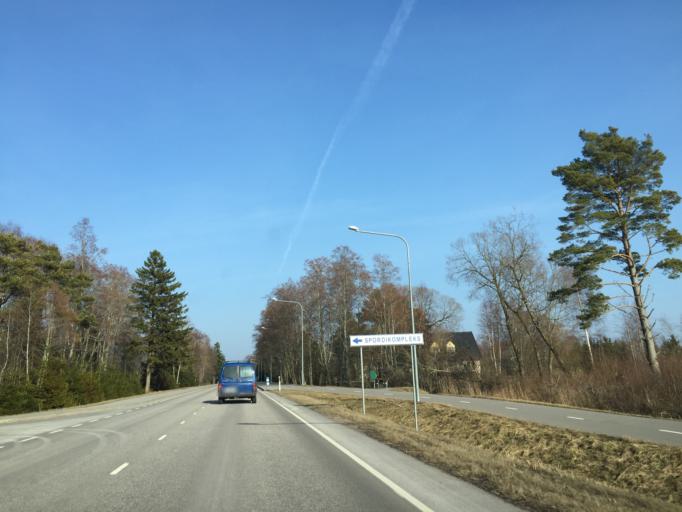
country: EE
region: Saare
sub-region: Kuressaare linn
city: Kuressaare
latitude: 58.2265
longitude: 22.3733
